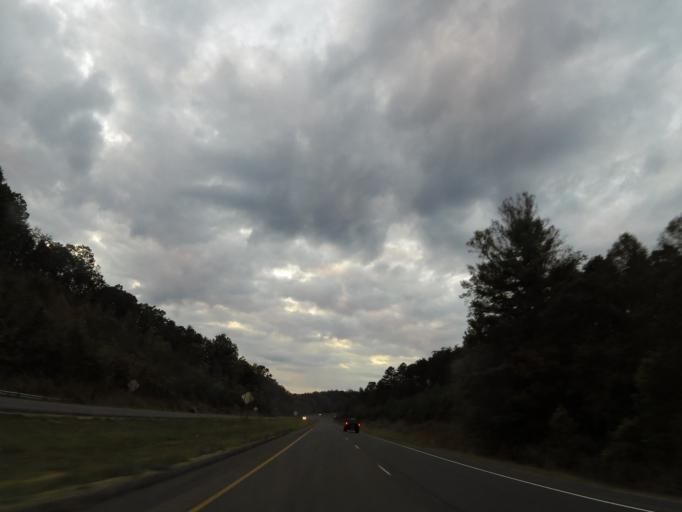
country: US
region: North Carolina
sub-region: Buncombe County
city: Weaverville
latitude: 35.7351
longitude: -82.6110
